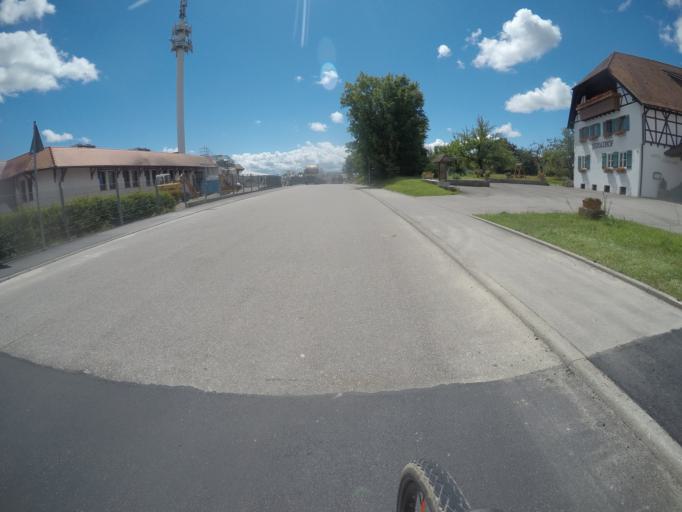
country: DE
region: Baden-Wuerttemberg
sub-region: Karlsruhe Region
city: Horb am Neckar
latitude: 48.4561
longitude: 8.6937
